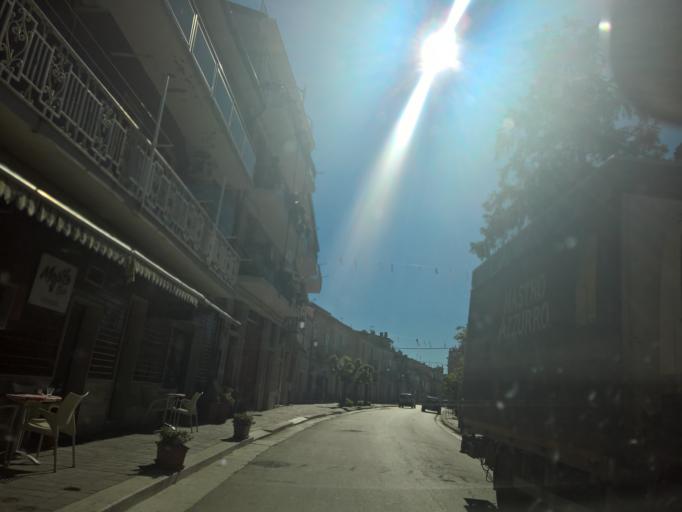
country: IT
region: Apulia
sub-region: Provincia di Foggia
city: Castelluccio Valmaggiore
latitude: 41.3425
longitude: 15.2009
